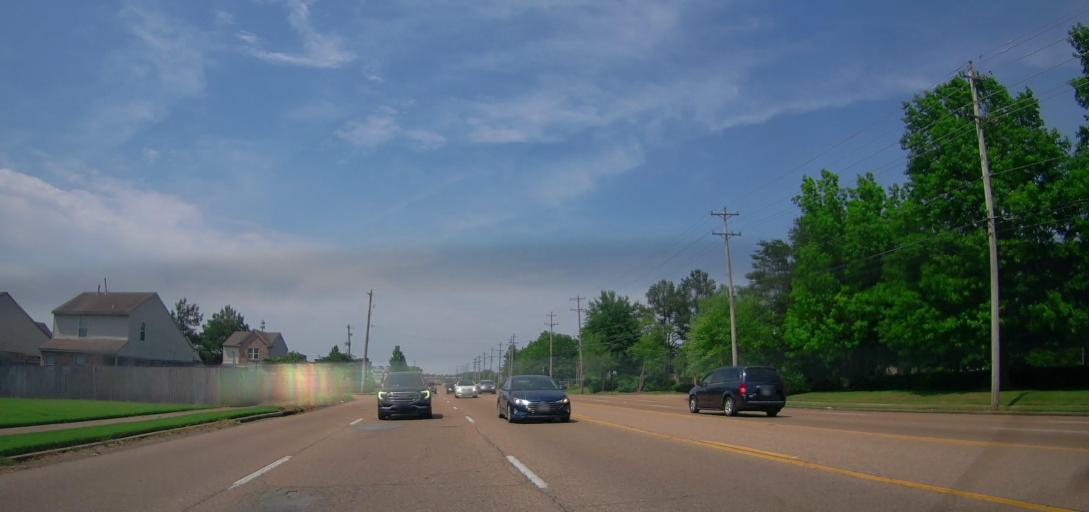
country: US
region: Tennessee
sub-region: Shelby County
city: Germantown
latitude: 35.0307
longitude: -89.7959
